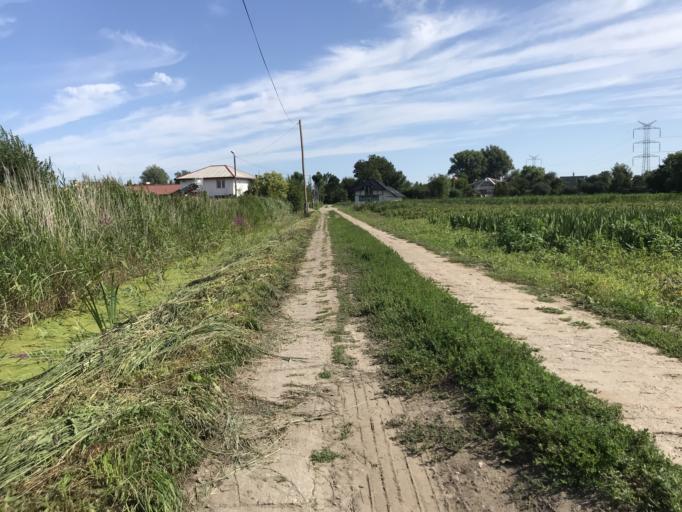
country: PL
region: Pomeranian Voivodeship
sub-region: Gdansk
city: Gdansk
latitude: 54.3198
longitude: 18.6768
